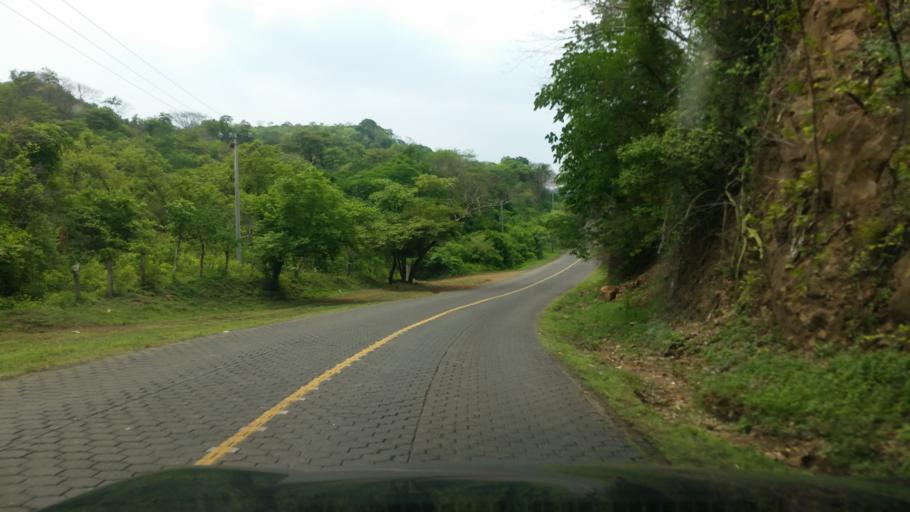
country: NI
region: Managua
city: Masachapa
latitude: 11.8602
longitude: -86.5193
